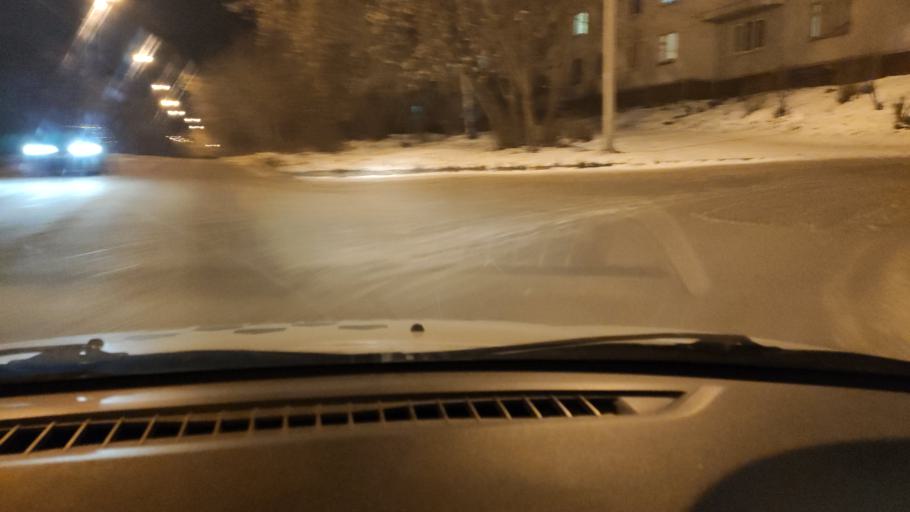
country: RU
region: Perm
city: Perm
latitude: 58.0995
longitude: 56.3043
